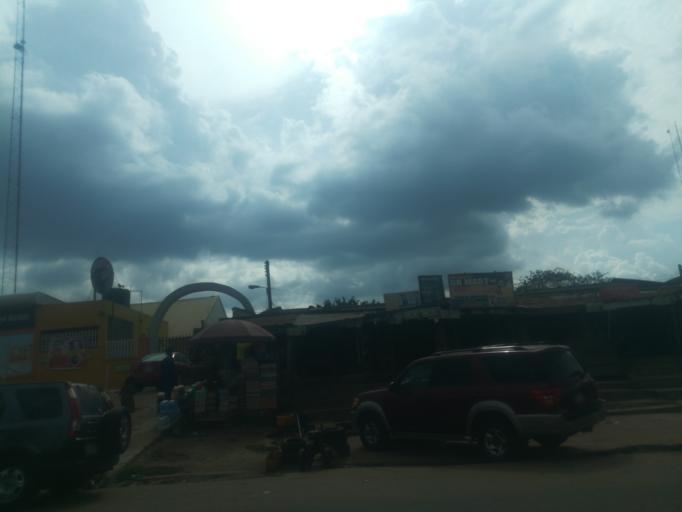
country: NG
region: Oyo
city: Ibadan
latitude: 7.4350
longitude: 3.9109
